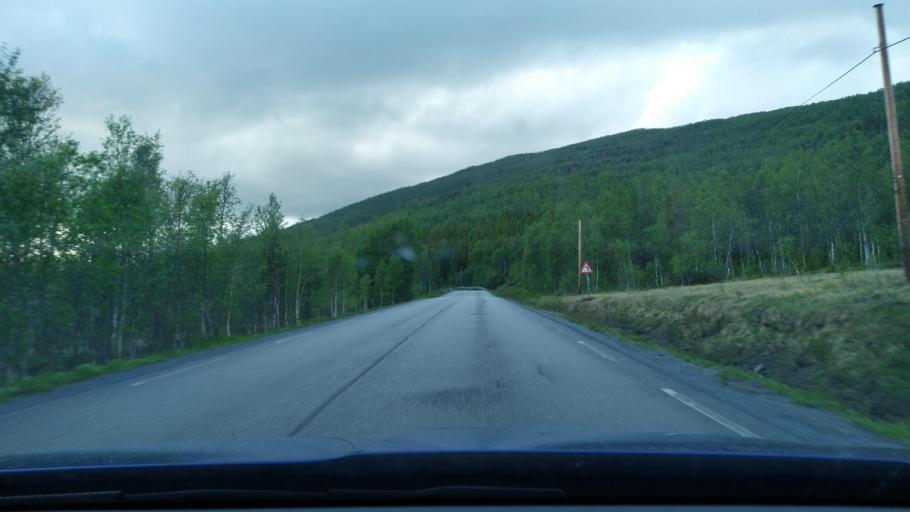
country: NO
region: Troms
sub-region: Dyroy
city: Brostadbotn
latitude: 69.0530
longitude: 17.8198
